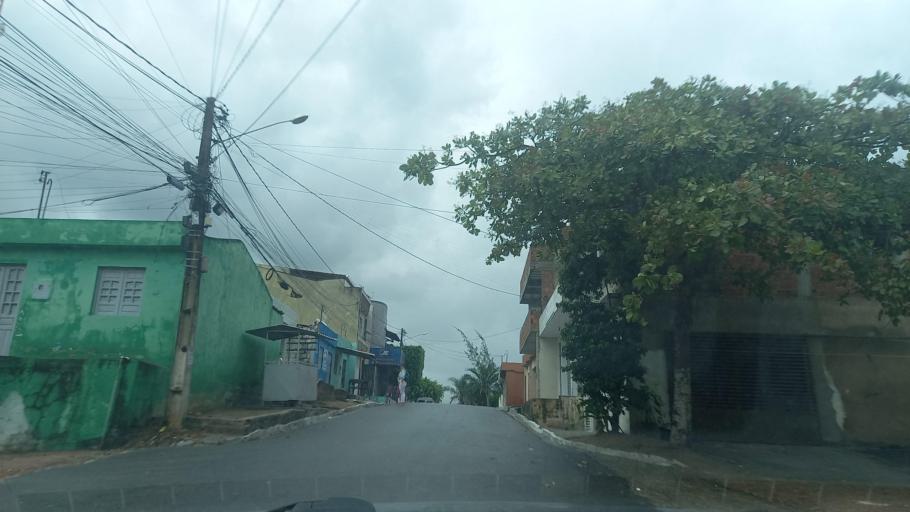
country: BR
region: Pernambuco
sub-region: Vitoria De Santo Antao
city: Vitoria de Santo Antao
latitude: -8.1297
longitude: -35.2874
